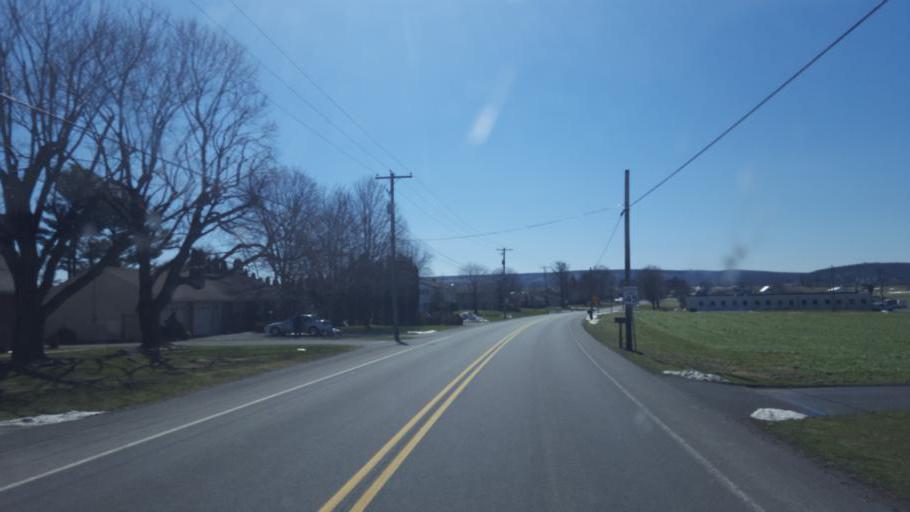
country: US
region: Pennsylvania
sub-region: Lancaster County
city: East Earl
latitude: 40.1351
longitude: -76.0268
